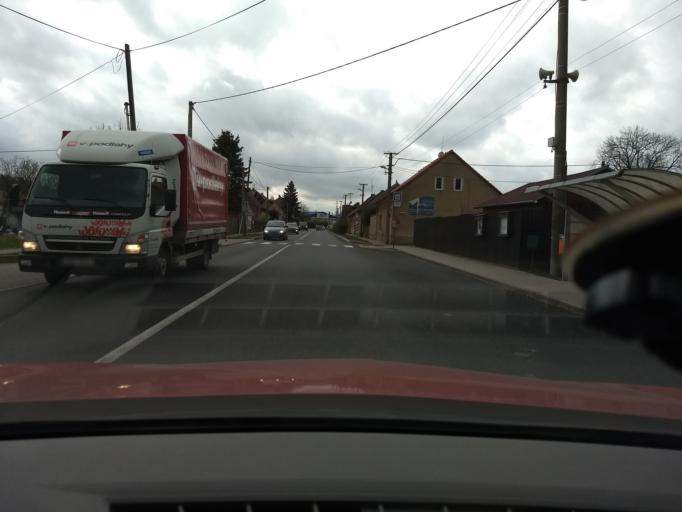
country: CZ
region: Central Bohemia
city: Unhost'
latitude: 50.1069
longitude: 14.1372
